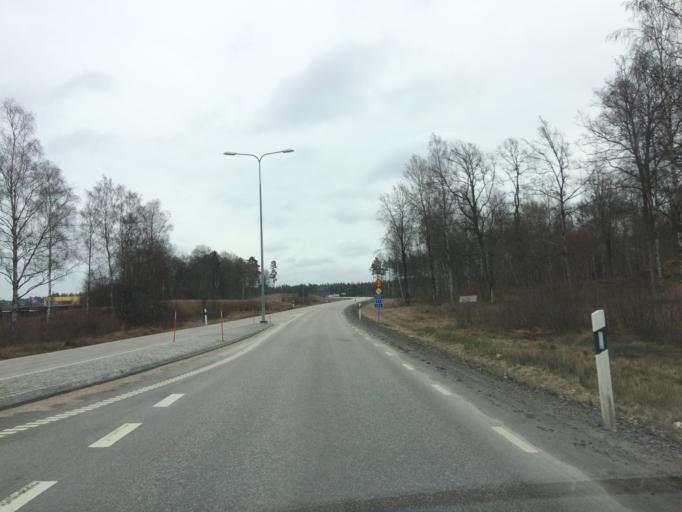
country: SE
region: Kronoberg
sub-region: Almhults Kommun
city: AElmhult
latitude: 56.5488
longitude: 14.1495
